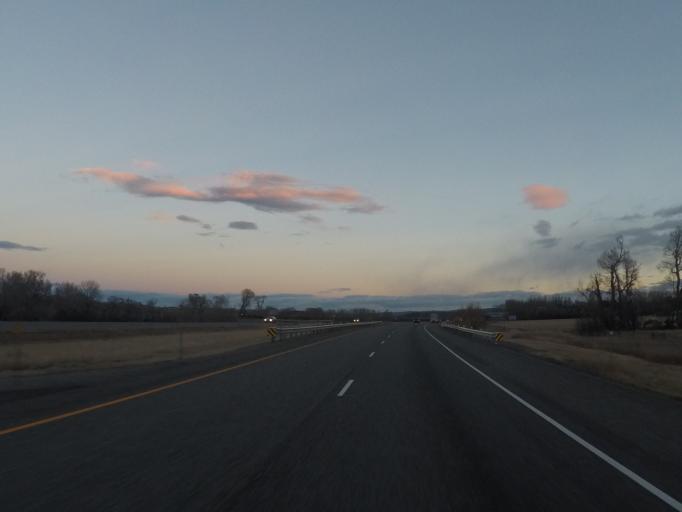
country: US
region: Montana
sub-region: Sweet Grass County
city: Big Timber
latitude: 45.7795
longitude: -109.8047
